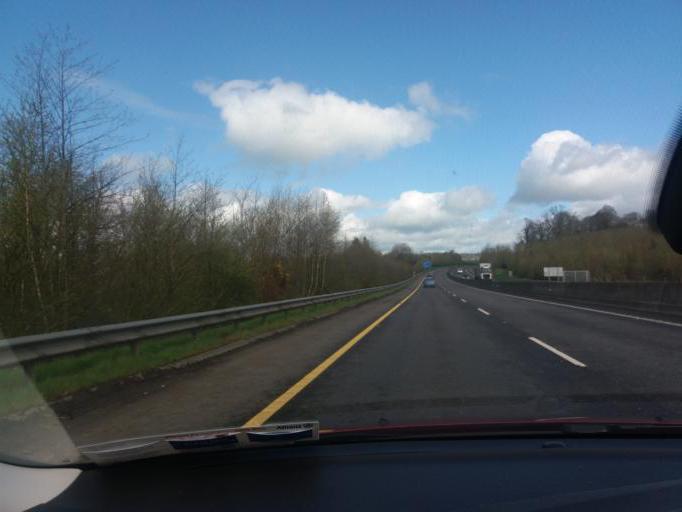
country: IE
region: Munster
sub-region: County Cork
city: Fermoy
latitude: 52.1699
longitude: -8.2693
